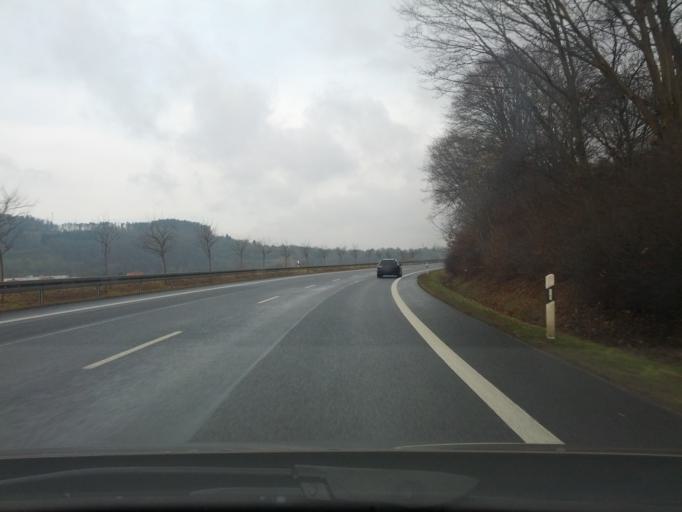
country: DE
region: Hesse
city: Witzenhausen
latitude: 51.3221
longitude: 9.8886
